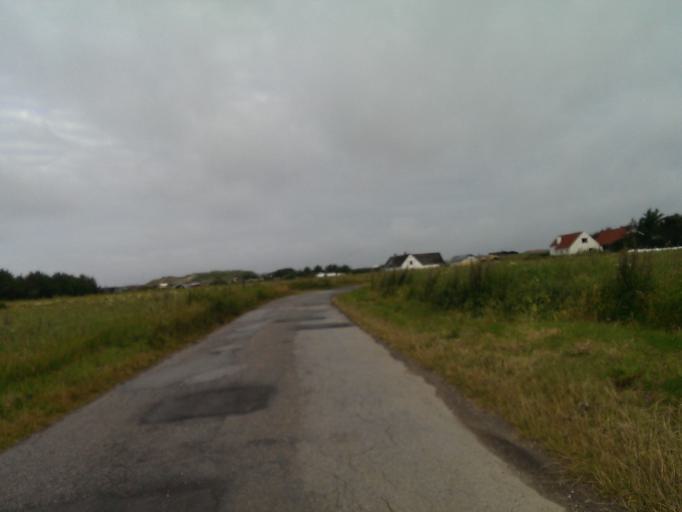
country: DK
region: North Denmark
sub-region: Jammerbugt Kommune
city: Pandrup
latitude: 57.3800
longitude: 9.7307
